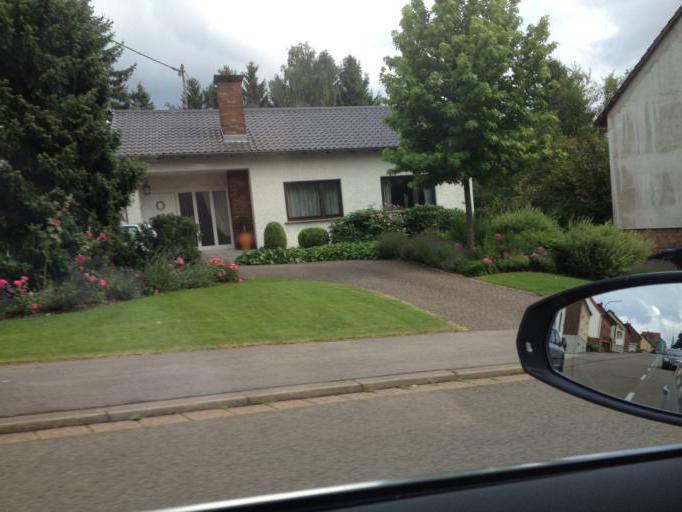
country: DE
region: Saarland
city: Schiffweiler
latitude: 49.3688
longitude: 7.1265
